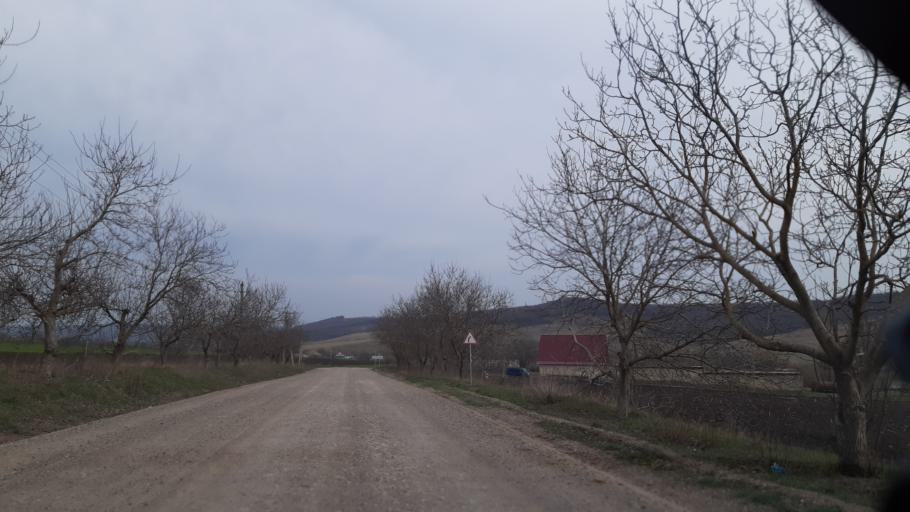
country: MD
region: Soldanesti
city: Soldanesti
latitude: 47.6895
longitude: 28.7427
